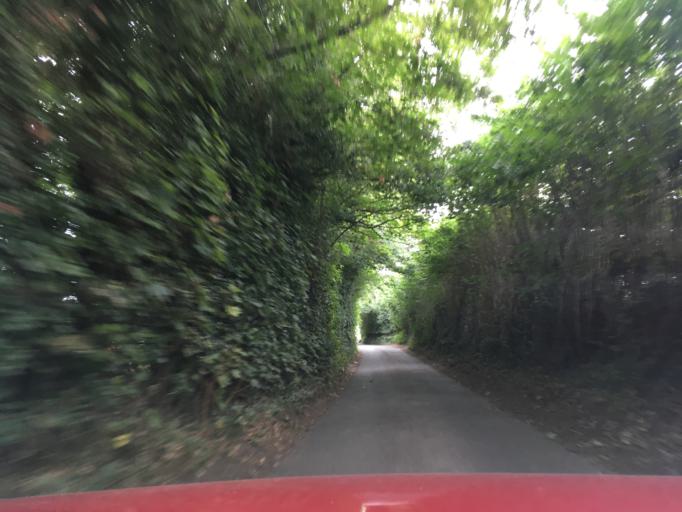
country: GB
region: England
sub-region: Kent
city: Maidstone
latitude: 51.2328
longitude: 0.5408
